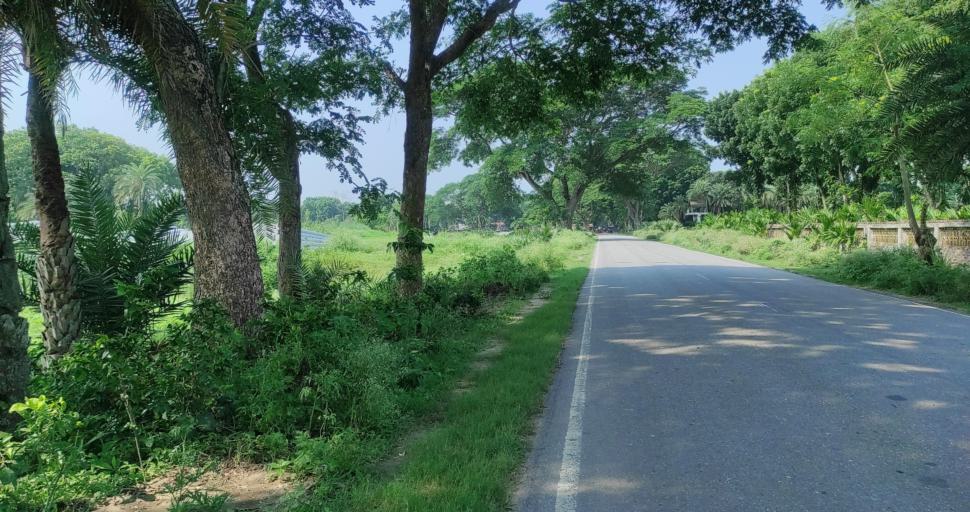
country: BD
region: Rajshahi
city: Ishurdi
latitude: 24.2773
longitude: 89.0582
